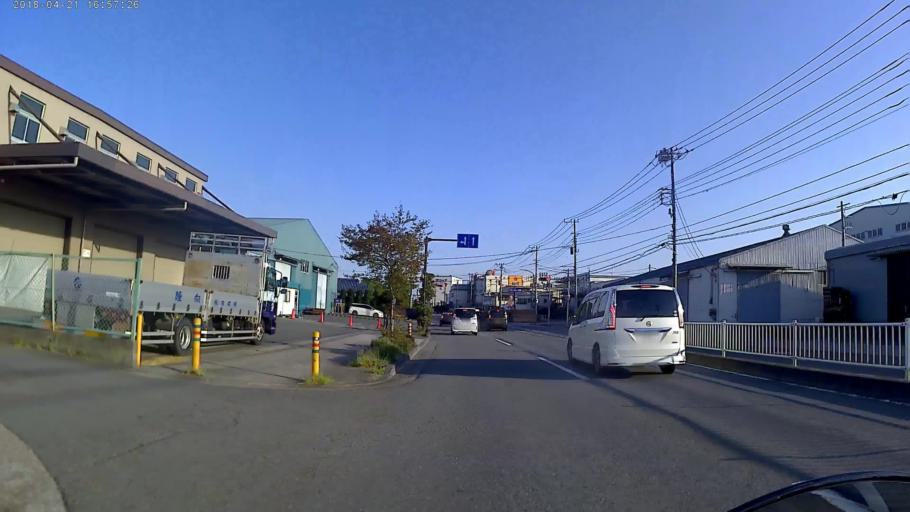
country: JP
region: Kanagawa
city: Minami-rinkan
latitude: 35.4533
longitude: 139.4179
